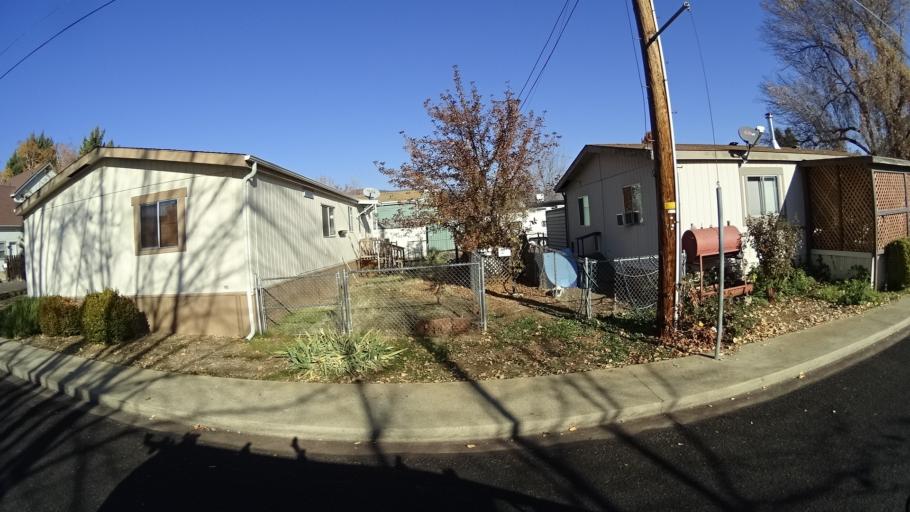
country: US
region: California
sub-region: Siskiyou County
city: Yreka
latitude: 41.7238
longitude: -122.6469
